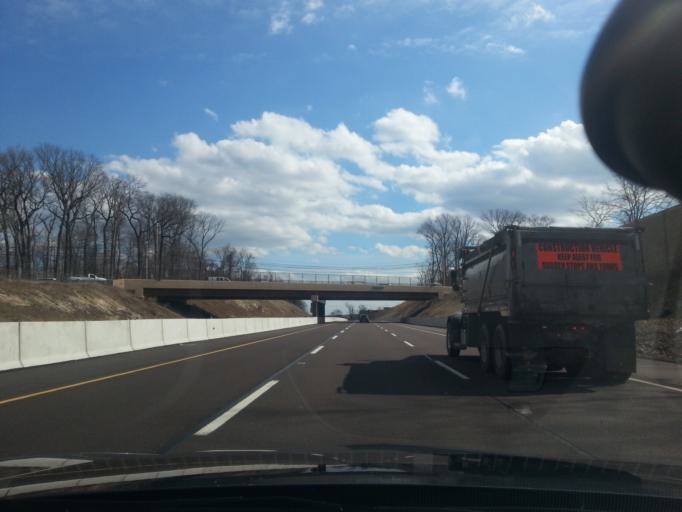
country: US
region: Pennsylvania
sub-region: Montgomery County
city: Plymouth Meeting
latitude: 40.1277
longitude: -75.2847
